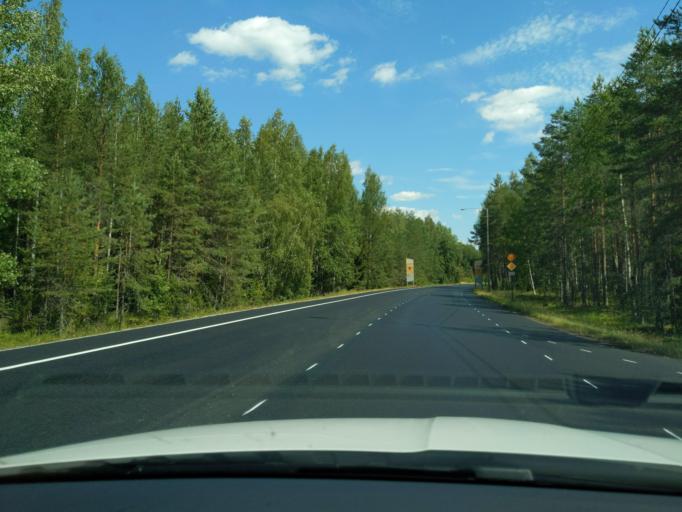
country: FI
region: Paijanne Tavastia
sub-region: Lahti
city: Heinola
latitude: 61.1050
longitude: 25.9220
